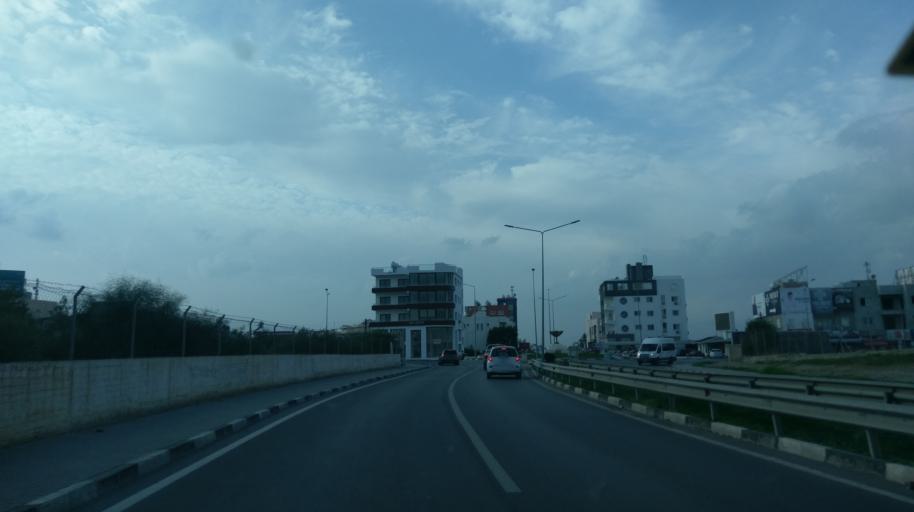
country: CY
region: Lefkosia
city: Nicosia
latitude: 35.1902
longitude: 33.3282
